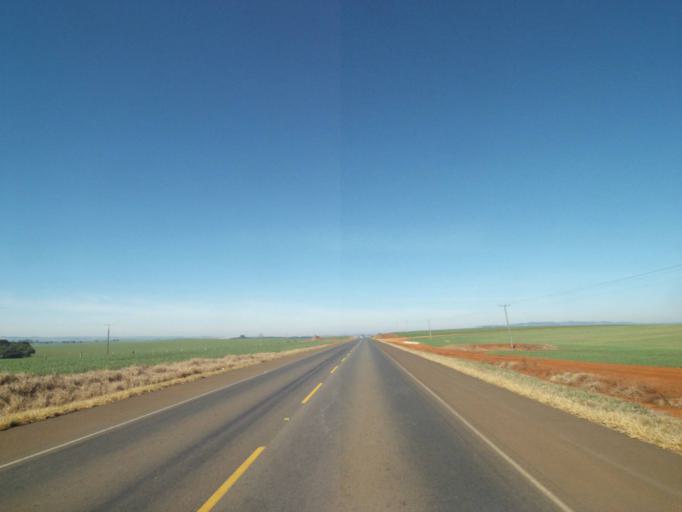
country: BR
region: Parana
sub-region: Tibagi
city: Tibagi
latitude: -24.4455
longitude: -50.4234
